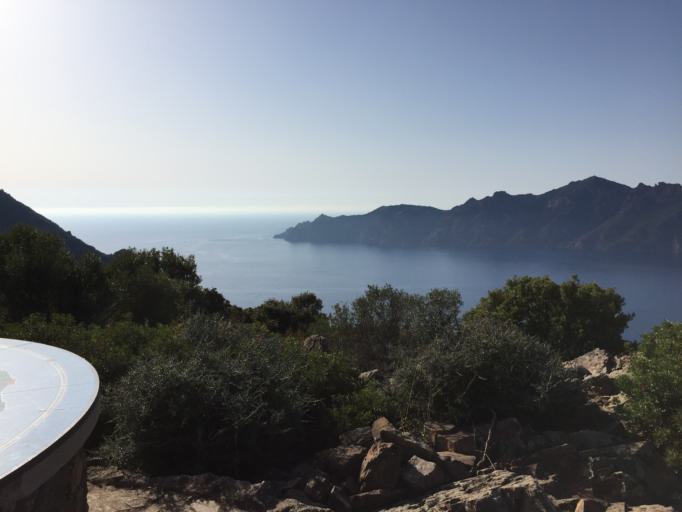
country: FR
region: Corsica
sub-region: Departement de la Corse-du-Sud
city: Cargese
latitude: 42.3252
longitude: 8.6289
